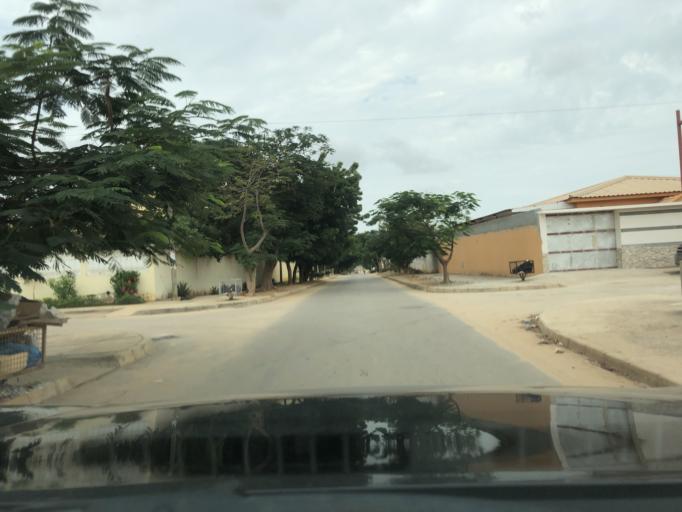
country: AO
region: Luanda
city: Luanda
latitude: -8.9355
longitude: 13.2467
